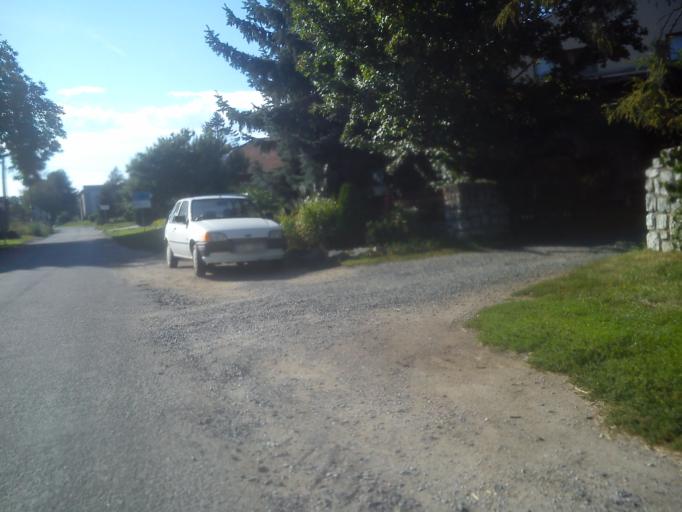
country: CZ
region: South Moravian
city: Sokolnice
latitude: 49.1081
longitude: 16.7370
